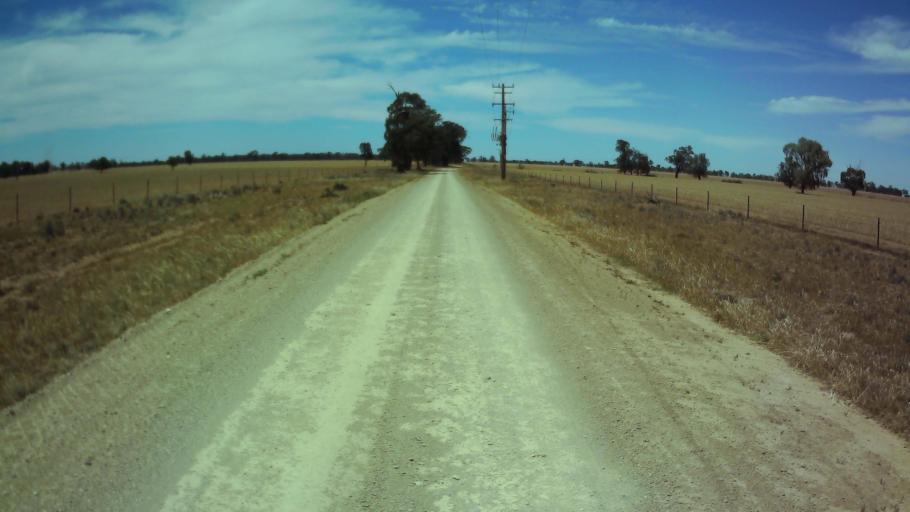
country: AU
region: New South Wales
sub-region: Weddin
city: Grenfell
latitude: -33.8856
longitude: 147.8036
